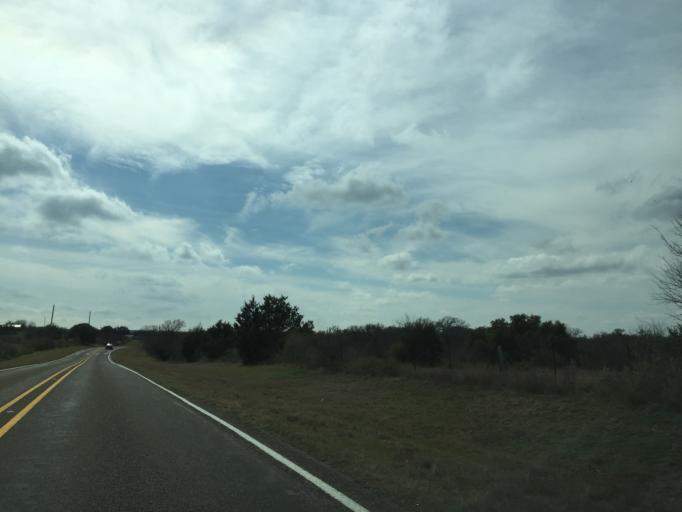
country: US
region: Texas
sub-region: Burnet County
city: Granite Shoals
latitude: 30.5314
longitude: -98.4454
